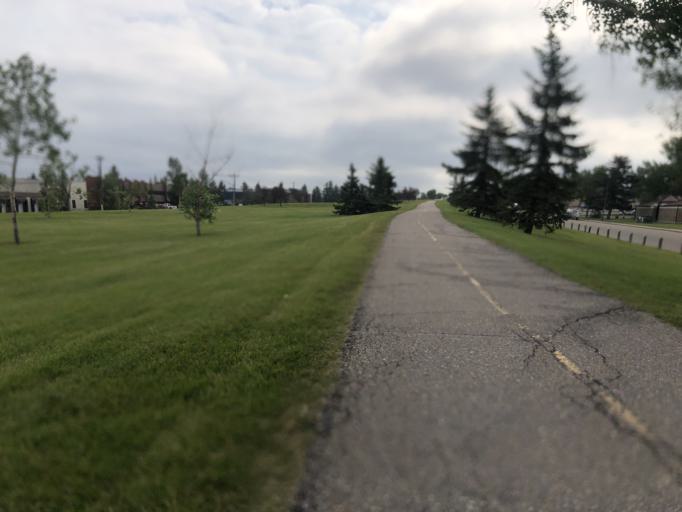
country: CA
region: Alberta
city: Calgary
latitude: 51.0744
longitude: -114.0184
